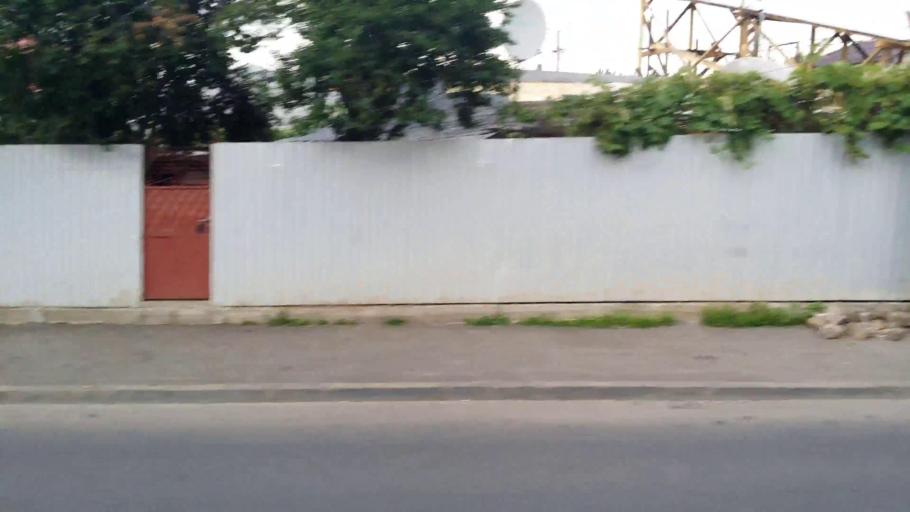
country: RO
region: Bucuresti
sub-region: Municipiul Bucuresti
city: Bucuresti
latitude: 44.3831
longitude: 26.0823
